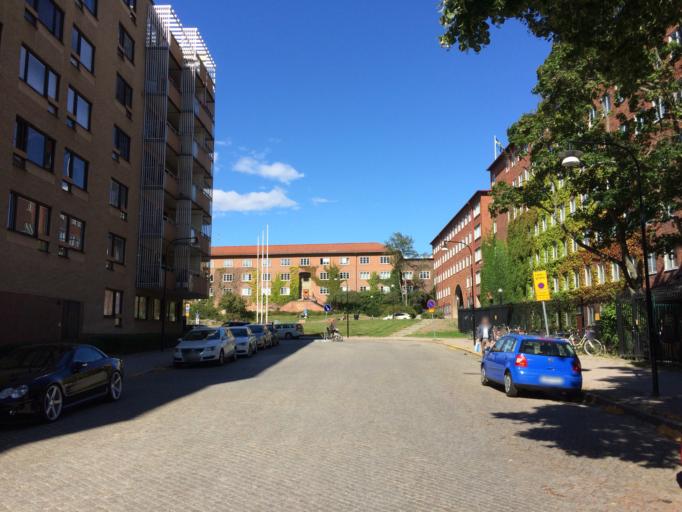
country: SE
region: Stockholm
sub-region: Stockholms Kommun
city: OEstermalm
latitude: 59.3407
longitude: 18.0977
